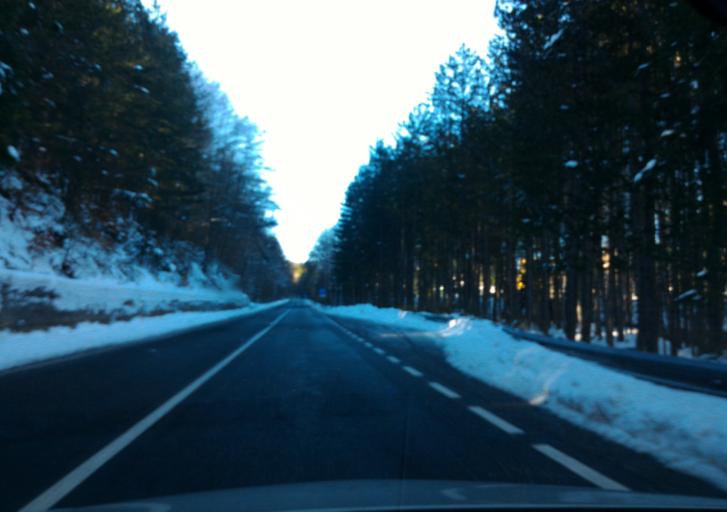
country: IT
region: Calabria
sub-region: Provincia di Cosenza
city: Celico
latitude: 39.3380
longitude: 16.4459
